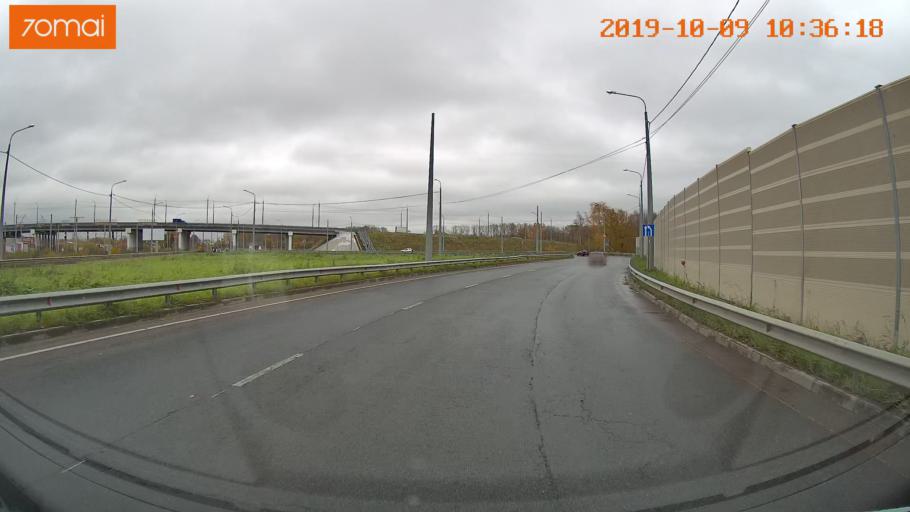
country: RU
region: Vologda
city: Vologda
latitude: 59.2322
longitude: 39.8648
